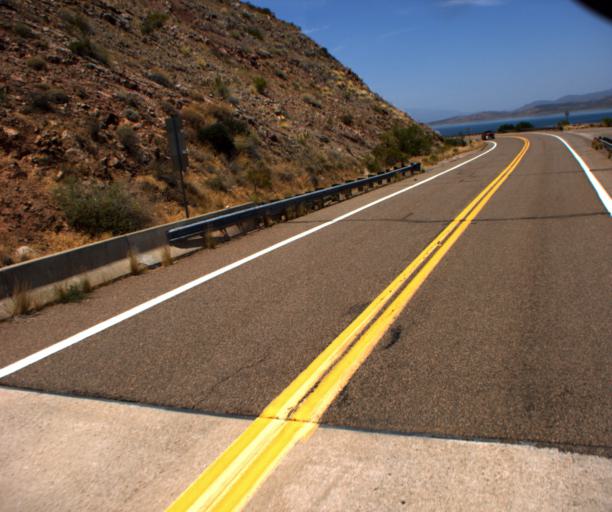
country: US
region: Arizona
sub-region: Gila County
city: Tonto Basin
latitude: 33.6764
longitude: -111.1608
